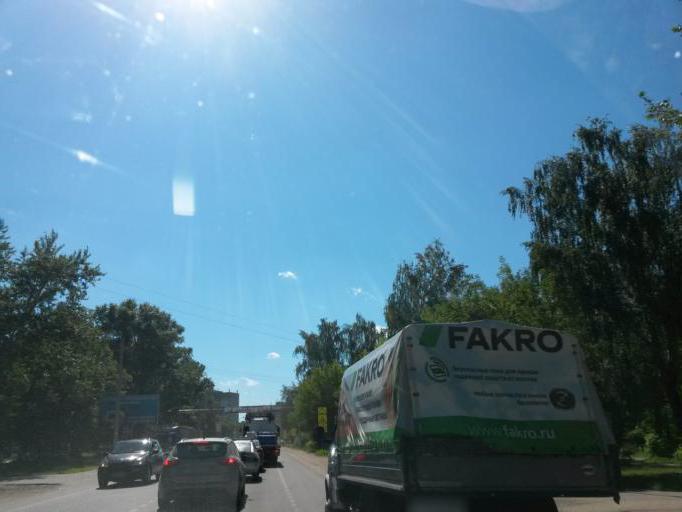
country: RU
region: Moskovskaya
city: Serpukhov
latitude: 54.9035
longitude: 37.3653
